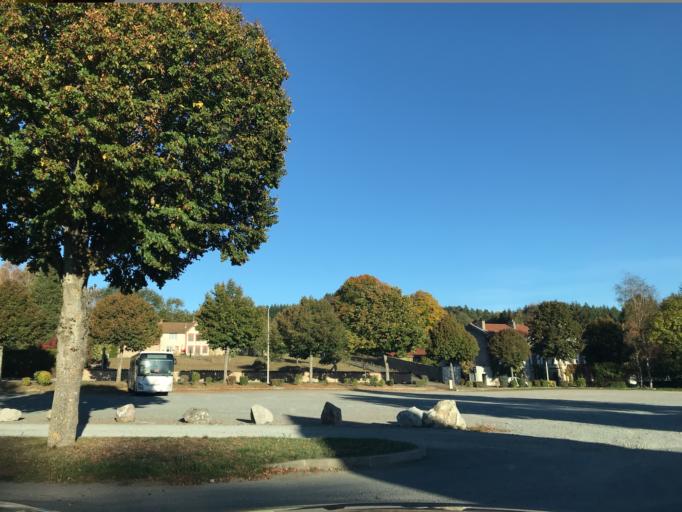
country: FR
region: Rhone-Alpes
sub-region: Departement de la Loire
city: Noiretable
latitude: 45.8142
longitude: 3.7685
